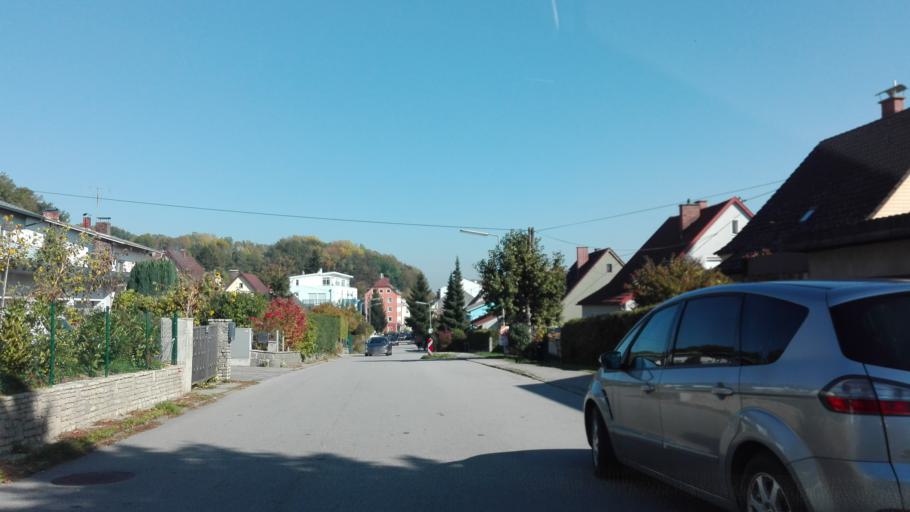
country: AT
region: Upper Austria
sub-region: Politischer Bezirk Linz-Land
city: Leonding
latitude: 48.2790
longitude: 14.2757
